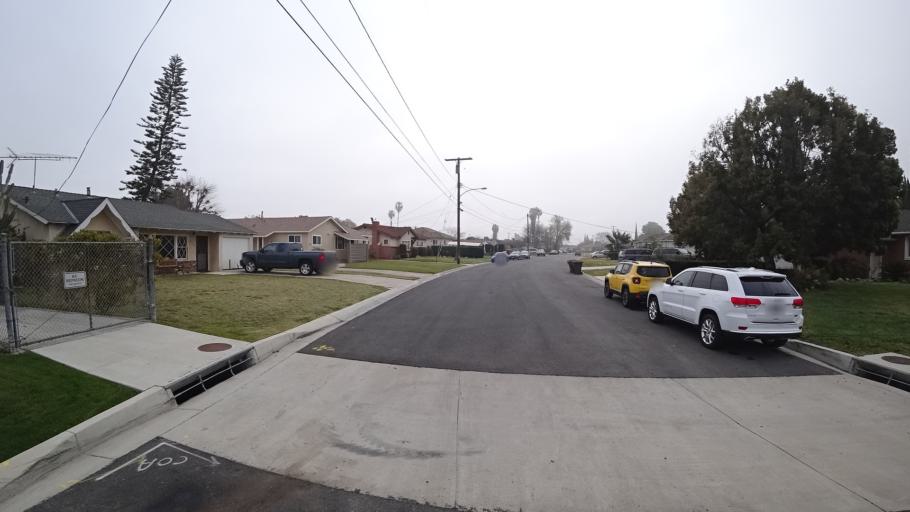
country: US
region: California
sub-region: Orange County
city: Stanton
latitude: 33.8132
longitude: -118.0065
